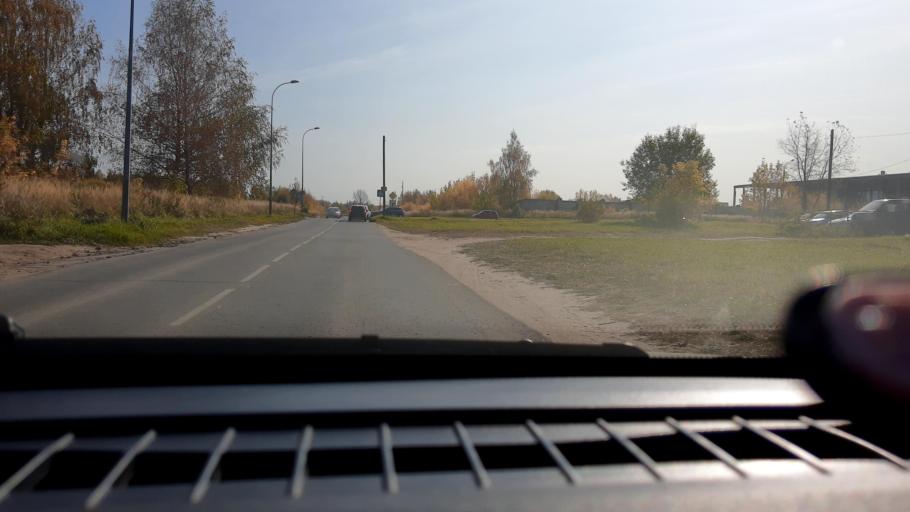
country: RU
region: Nizjnij Novgorod
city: Kstovo
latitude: 56.1514
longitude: 44.2214
